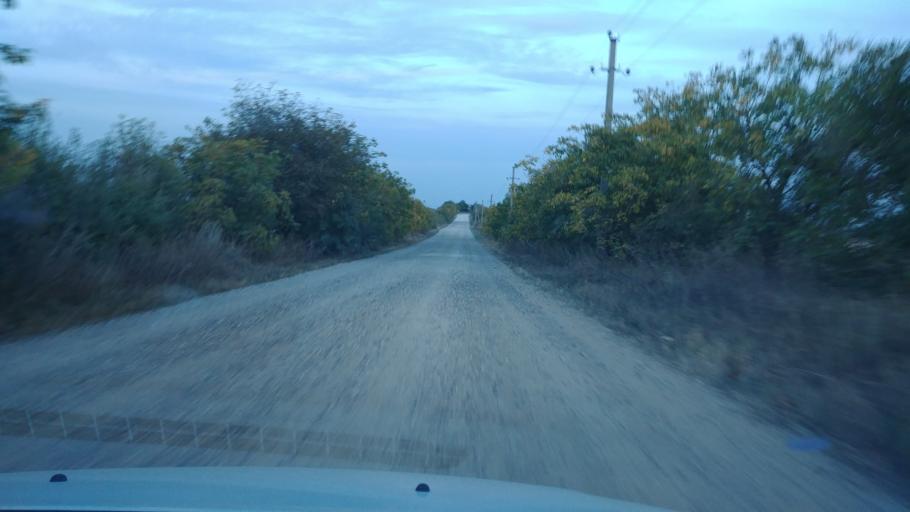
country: MD
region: Rezina
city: Saharna
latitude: 47.6812
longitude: 28.9097
